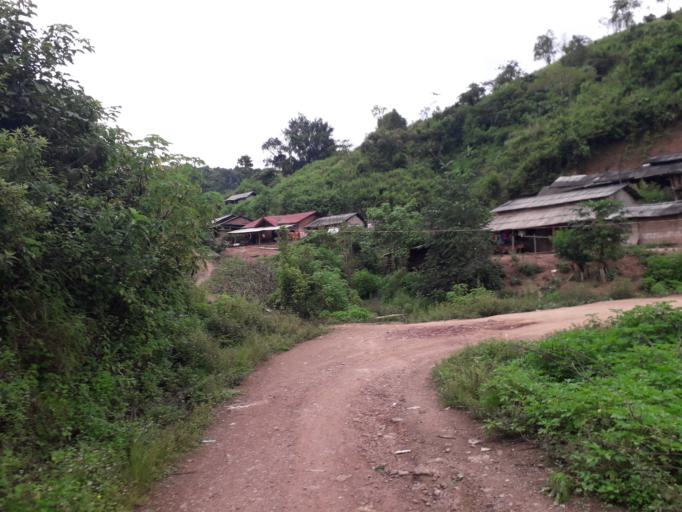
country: CN
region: Yunnan
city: Menglie
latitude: 22.2486
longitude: 101.6066
